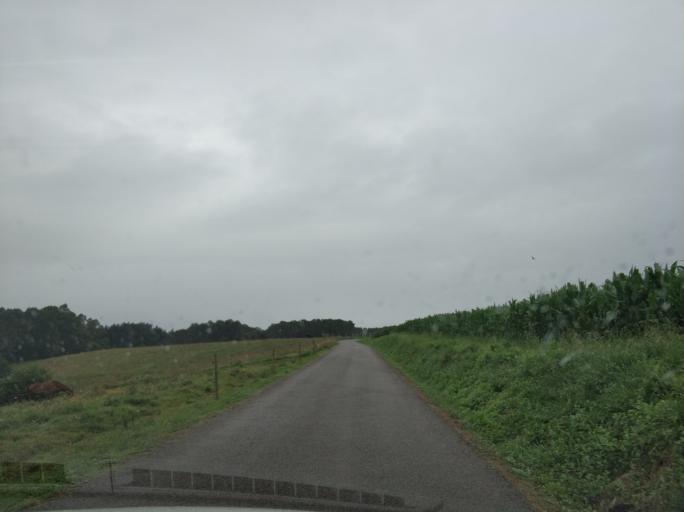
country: ES
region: Asturias
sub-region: Province of Asturias
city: Tineo
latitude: 43.5587
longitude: -6.4675
